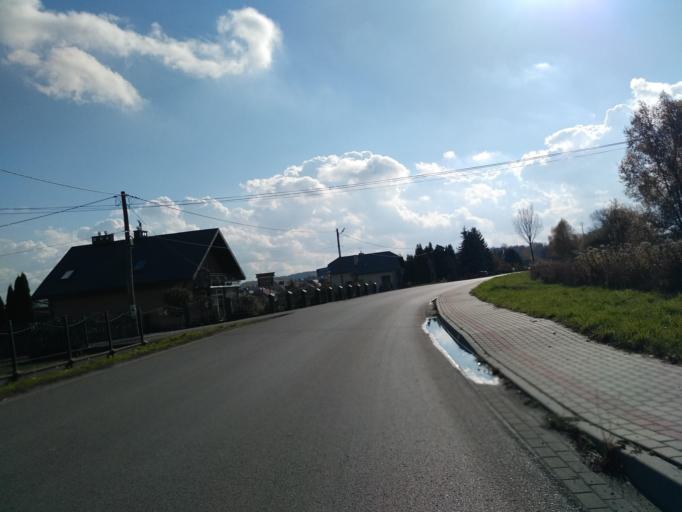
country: PL
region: Subcarpathian Voivodeship
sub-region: Powiat rzeszowski
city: Trzciana
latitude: 50.0842
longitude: 21.8403
